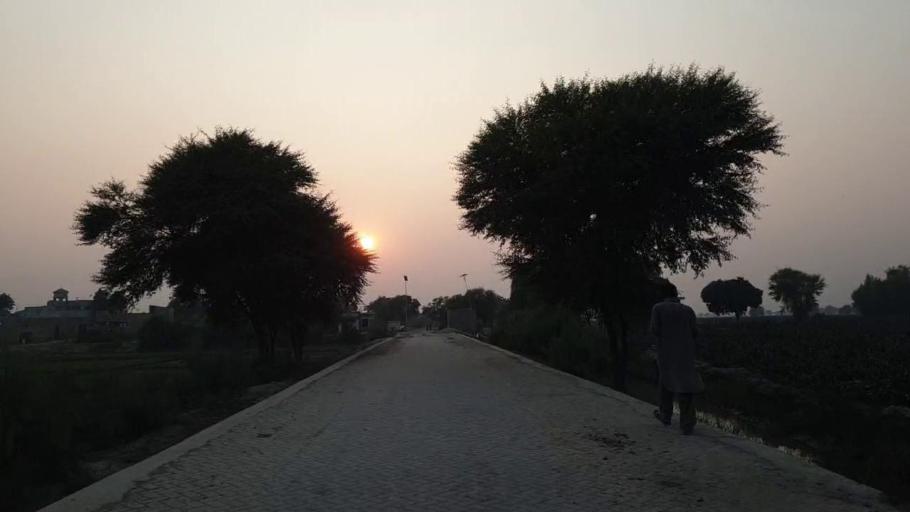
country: PK
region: Sindh
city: Bhan
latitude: 26.5225
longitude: 67.7122
